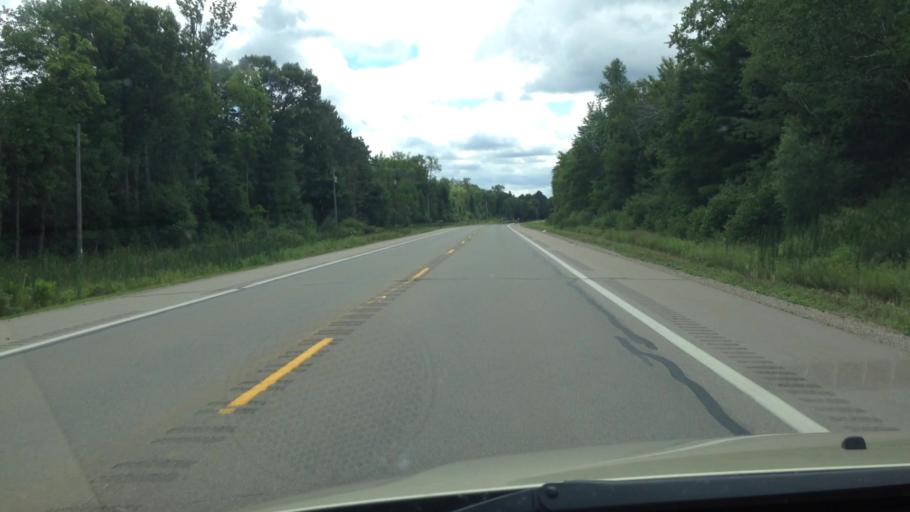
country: US
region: Michigan
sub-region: Menominee County
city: Menominee
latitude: 45.2245
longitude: -87.5137
